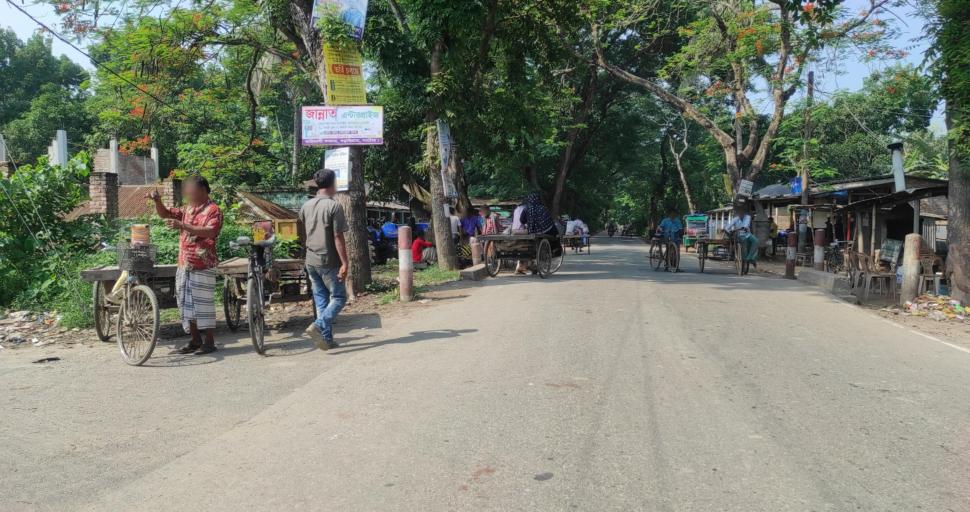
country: BD
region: Rajshahi
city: Ishurdi
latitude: 24.2742
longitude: 89.0567
